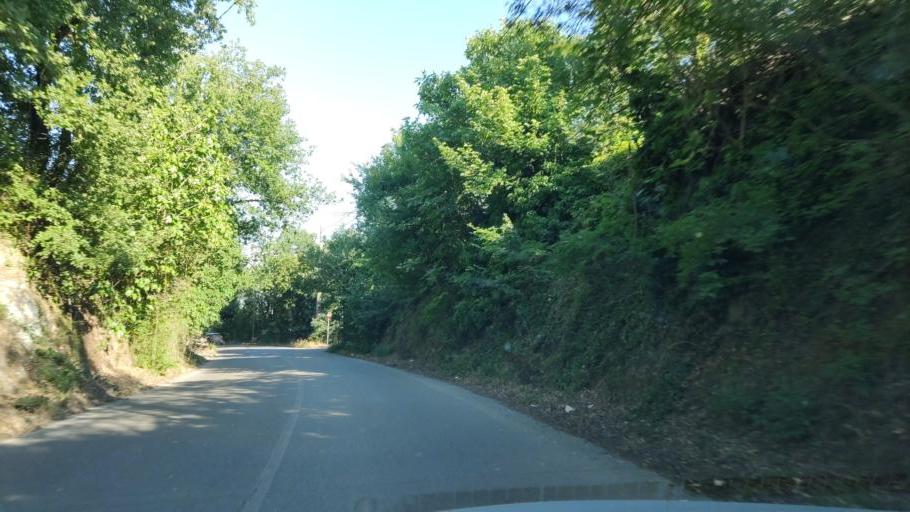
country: IT
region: Latium
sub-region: Provincia di Viterbo
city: Orte
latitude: 42.4704
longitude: 12.3707
